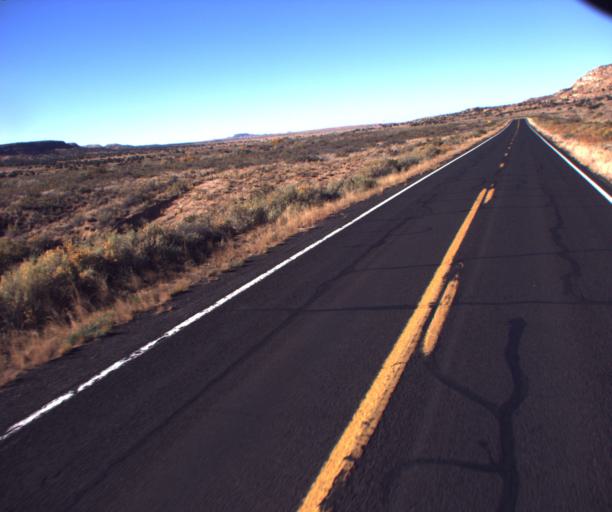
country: US
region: Arizona
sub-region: Navajo County
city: First Mesa
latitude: 35.8415
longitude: -110.2484
